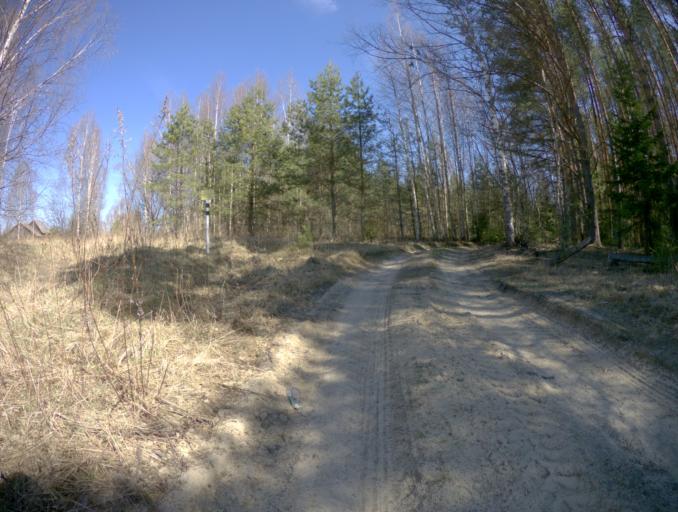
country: RU
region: Vladimir
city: Ivanishchi
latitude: 55.8500
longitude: 40.4468
